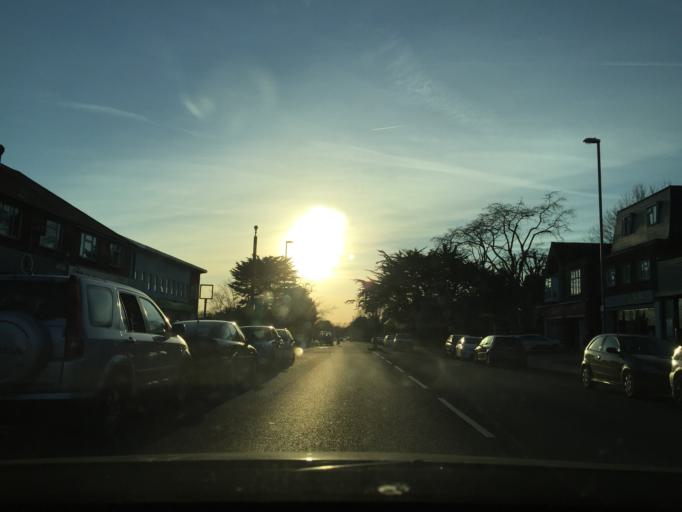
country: GB
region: England
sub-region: Portsmouth
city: Cosham
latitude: 50.8467
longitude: -1.0492
